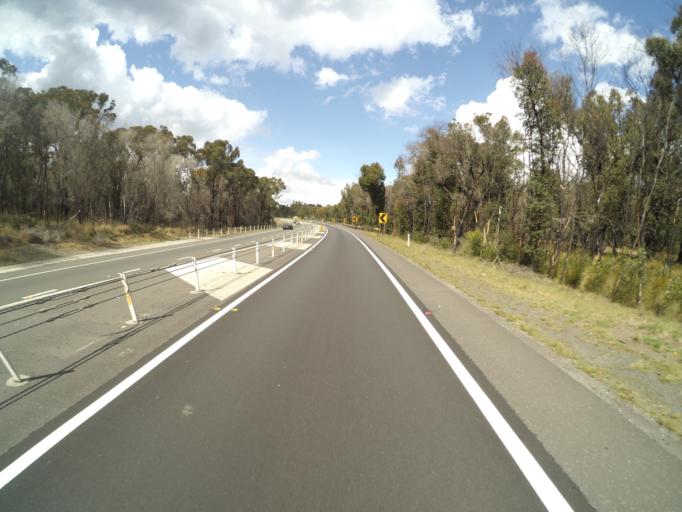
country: AU
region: New South Wales
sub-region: Wollondilly
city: Douglas Park
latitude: -34.3074
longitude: 150.7383
